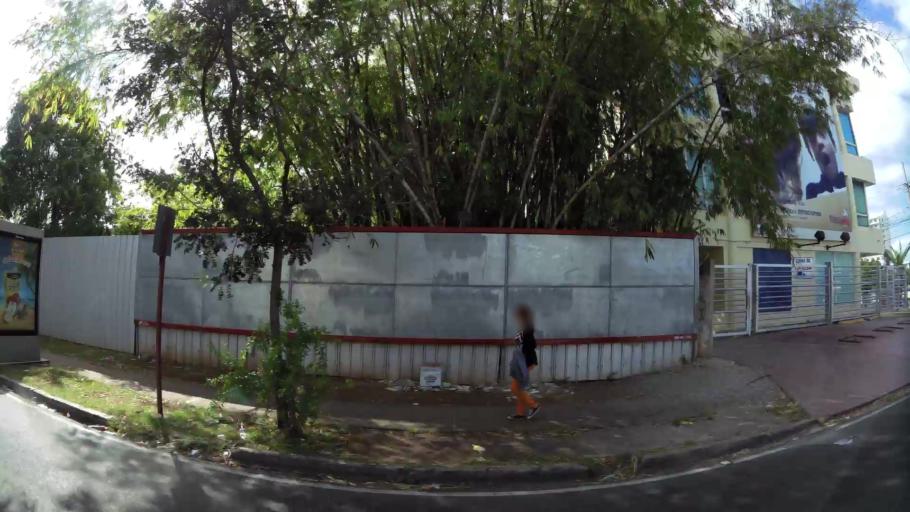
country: DO
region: Nacional
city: La Julia
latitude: 18.4605
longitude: -69.9335
